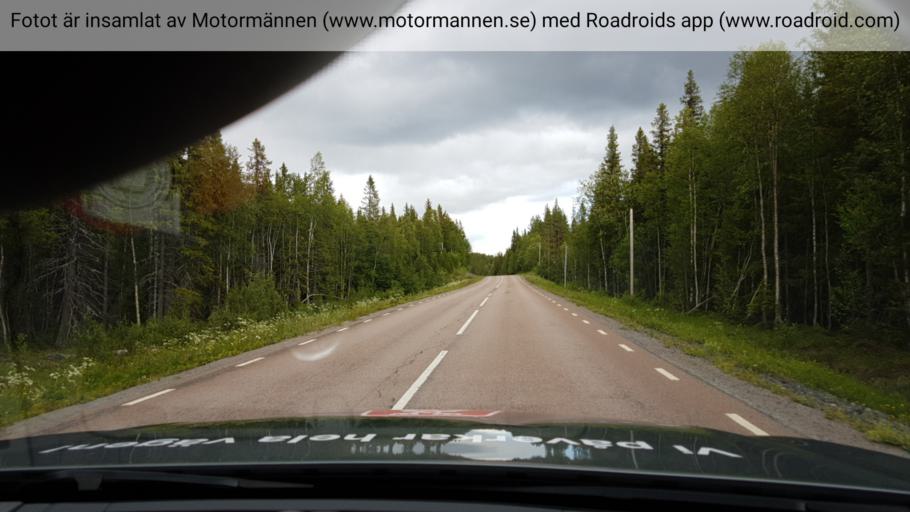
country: SE
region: Jaemtland
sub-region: Krokoms Kommun
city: Valla
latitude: 63.1134
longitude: 13.8972
